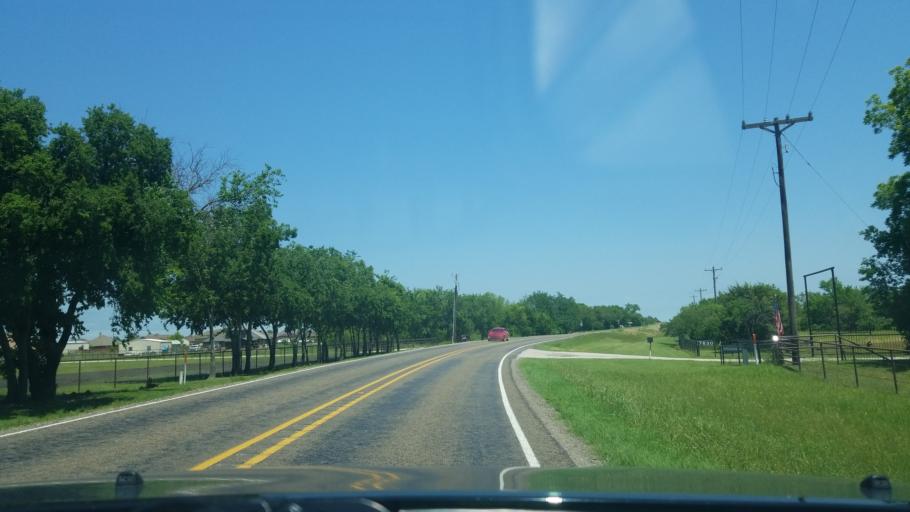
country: US
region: Texas
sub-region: Denton County
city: Krum
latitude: 33.3199
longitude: -97.2388
